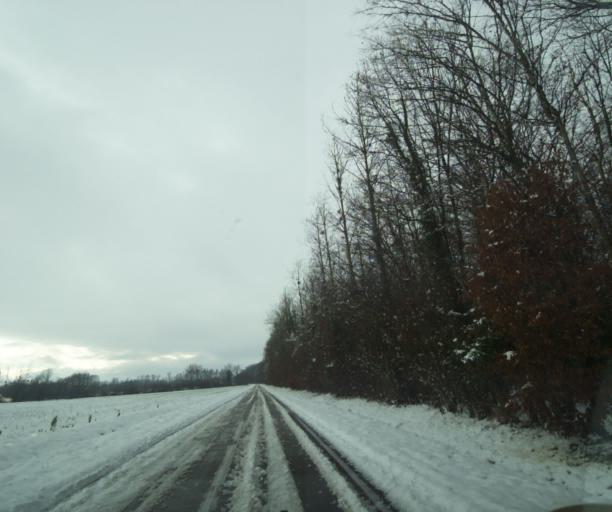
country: FR
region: Champagne-Ardenne
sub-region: Departement de la Haute-Marne
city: Montier-en-Der
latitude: 48.4791
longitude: 4.6653
